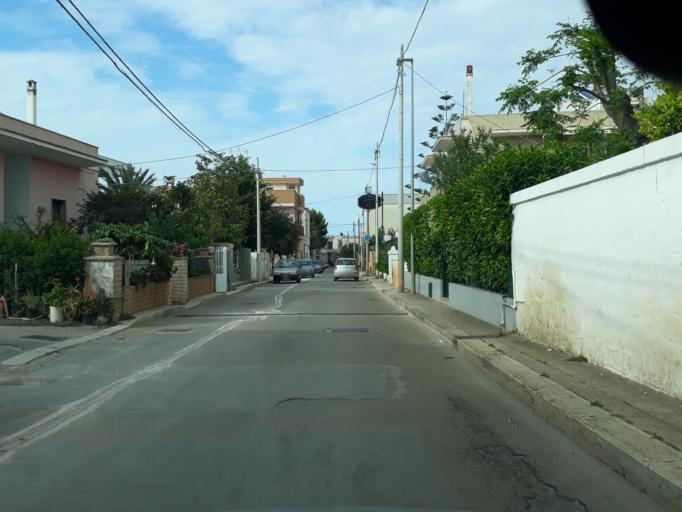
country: IT
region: Apulia
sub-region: Provincia di Brindisi
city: Pezze di Greco
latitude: 40.8094
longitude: 17.4136
